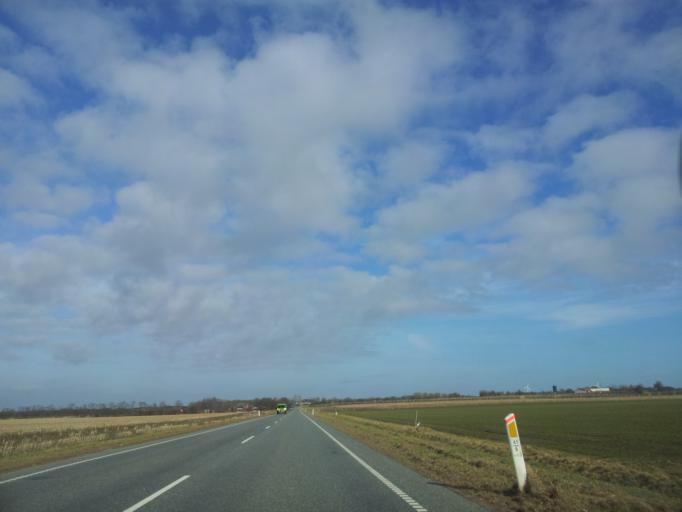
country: DK
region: South Denmark
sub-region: Vejen Kommune
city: Holsted
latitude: 55.3977
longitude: 8.9124
